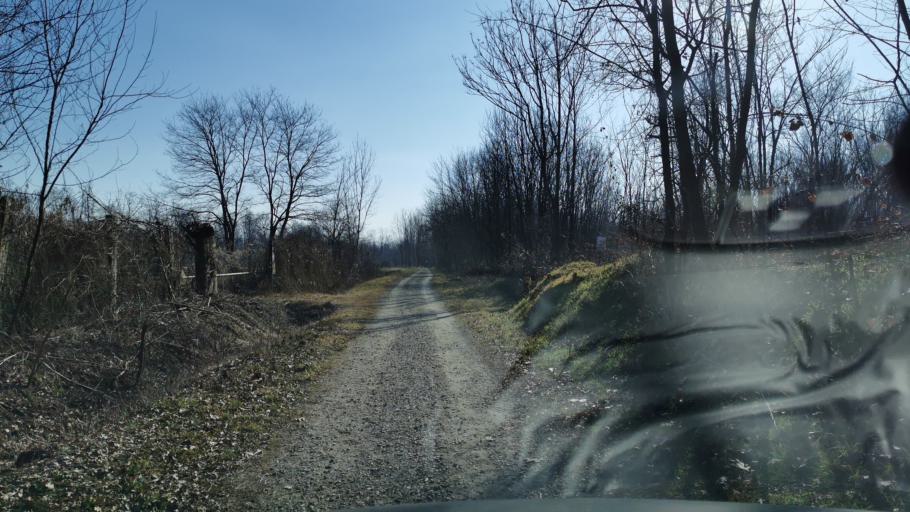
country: IT
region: Piedmont
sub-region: Provincia di Torino
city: Robassomero
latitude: 45.2164
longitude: 7.5684
